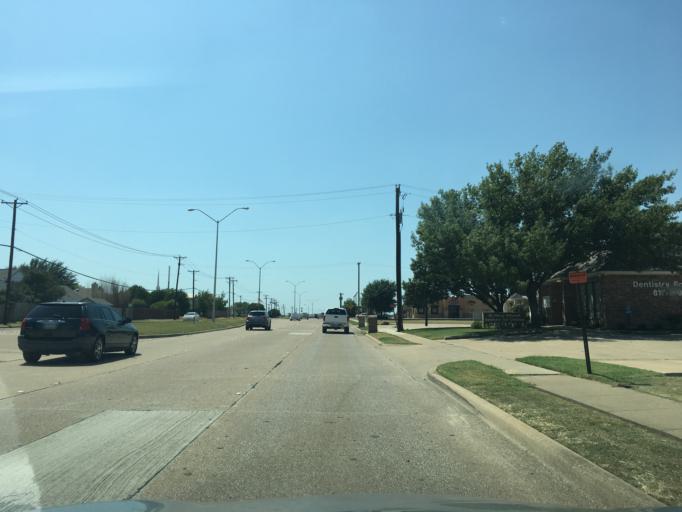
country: US
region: Texas
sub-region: Tarrant County
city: Edgecliff Village
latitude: 32.6350
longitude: -97.3649
